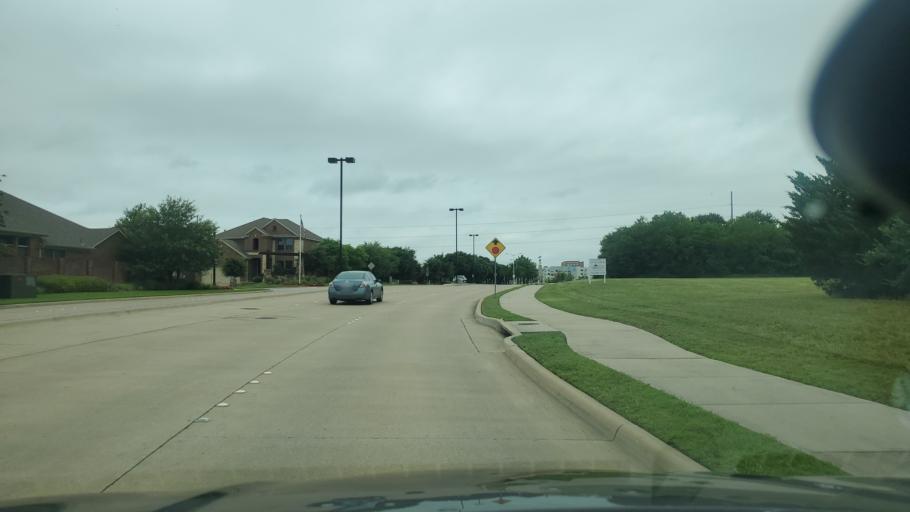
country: US
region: Texas
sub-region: Dallas County
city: Sachse
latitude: 32.9563
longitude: -96.6338
